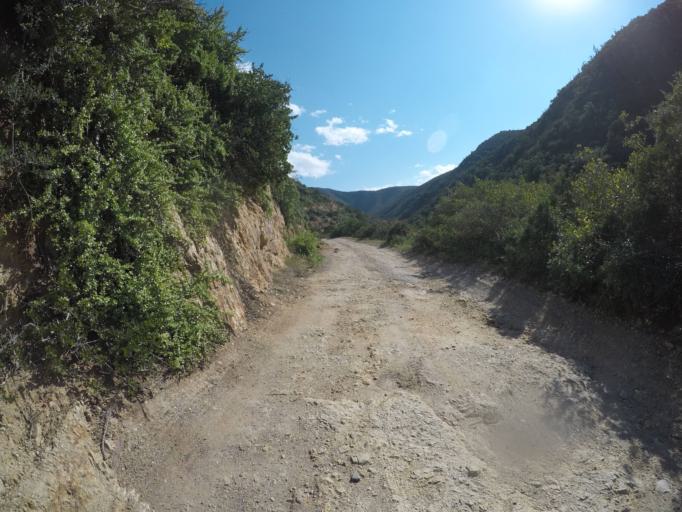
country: ZA
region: Eastern Cape
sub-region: Cacadu District Municipality
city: Kareedouw
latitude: -33.6556
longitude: 24.3602
